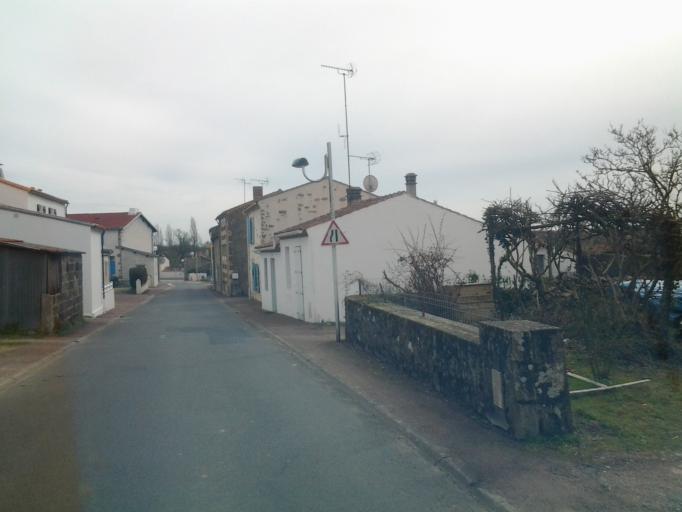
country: FR
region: Pays de la Loire
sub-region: Departement de la Vendee
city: Venansault
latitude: 46.6857
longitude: -1.5153
